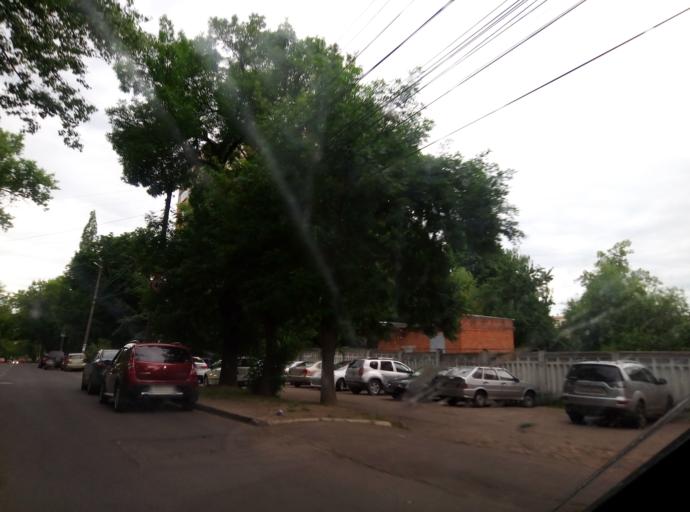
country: RU
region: Kursk
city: Kursk
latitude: 51.7458
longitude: 36.1870
